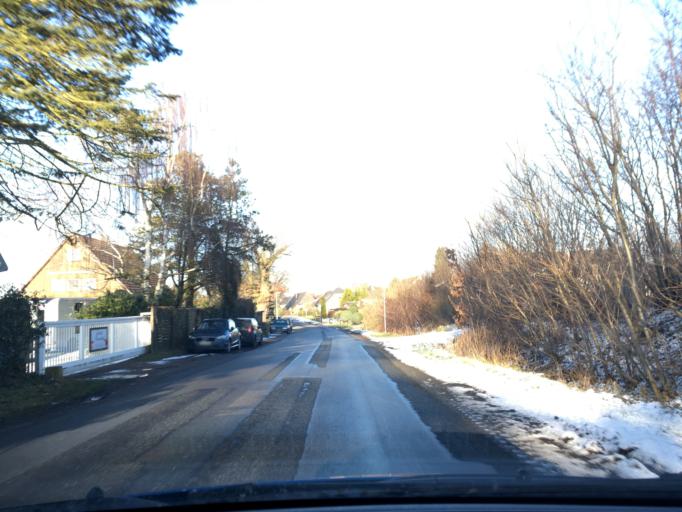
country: DE
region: Schleswig-Holstein
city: Schulendorf
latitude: 53.4697
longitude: 10.5662
